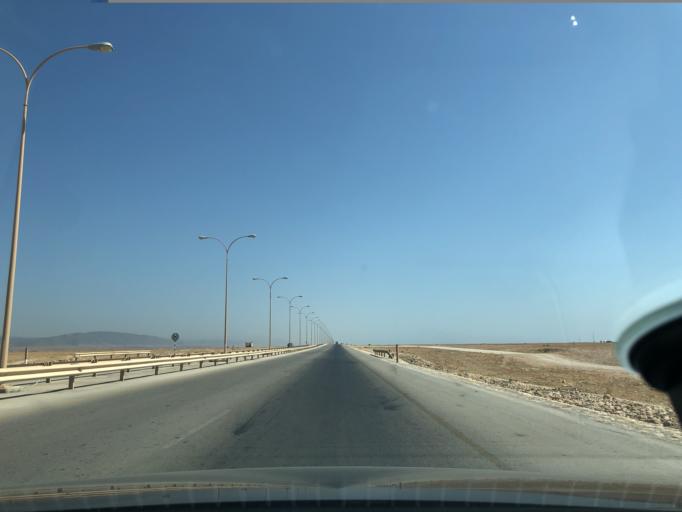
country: OM
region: Zufar
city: Salalah
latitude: 17.0499
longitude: 54.2291
